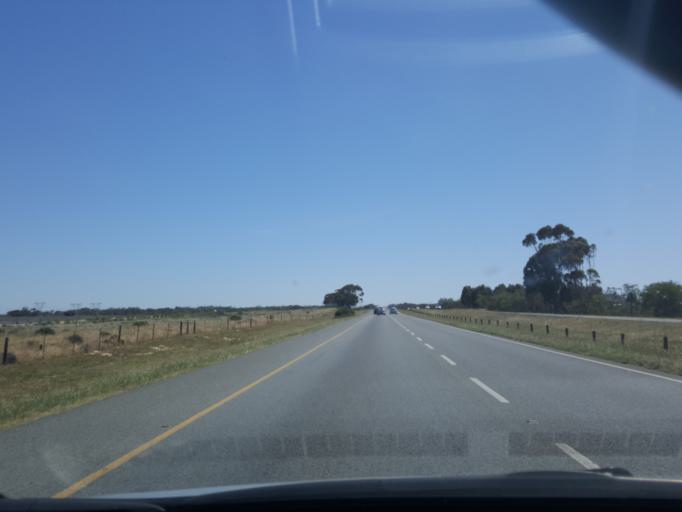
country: ZA
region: Western Cape
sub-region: City of Cape Town
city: Sunset Beach
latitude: -33.7664
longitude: 18.5476
